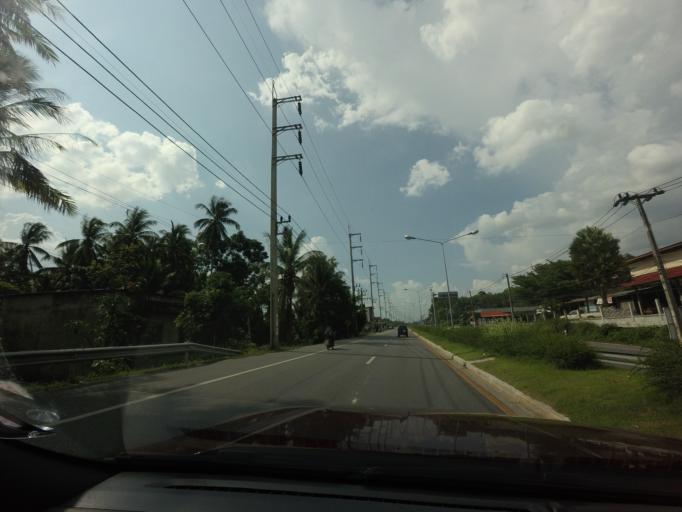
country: TH
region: Yala
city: Yala
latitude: 6.4936
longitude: 101.2650
